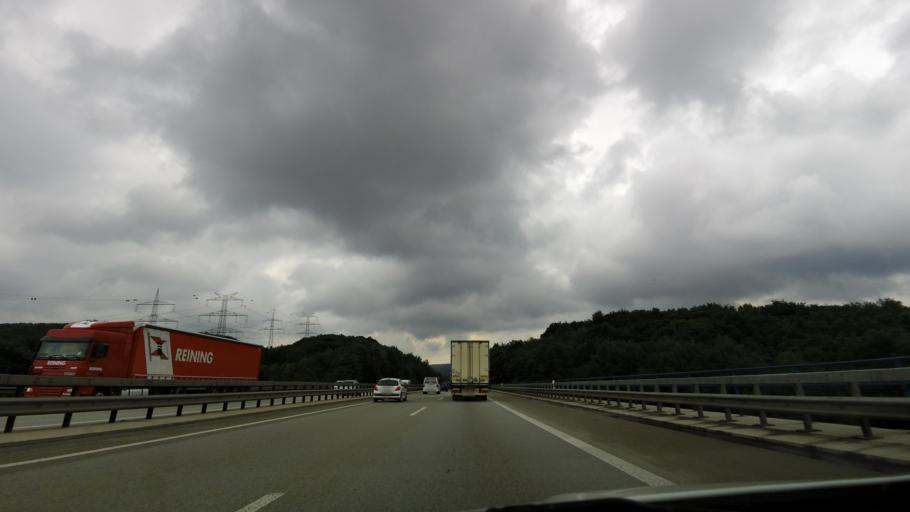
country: DE
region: Rheinland-Pfalz
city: Bad Neuenahr-Ahrweiler
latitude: 50.5631
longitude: 7.1459
